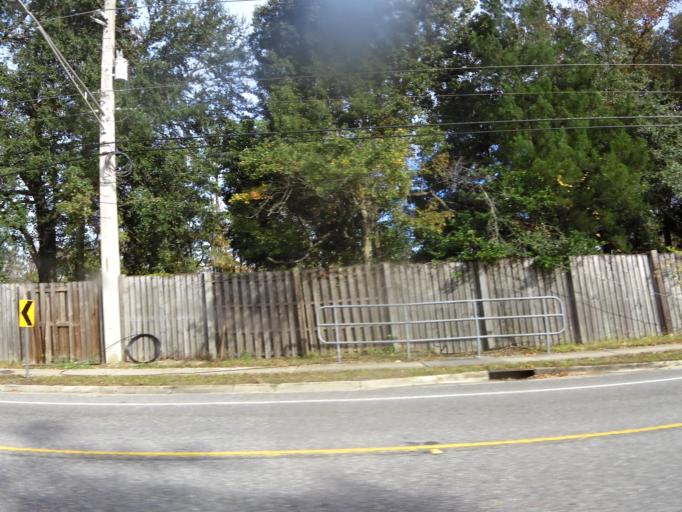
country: US
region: Florida
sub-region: Duval County
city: Jacksonville
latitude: 30.2309
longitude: -81.5975
